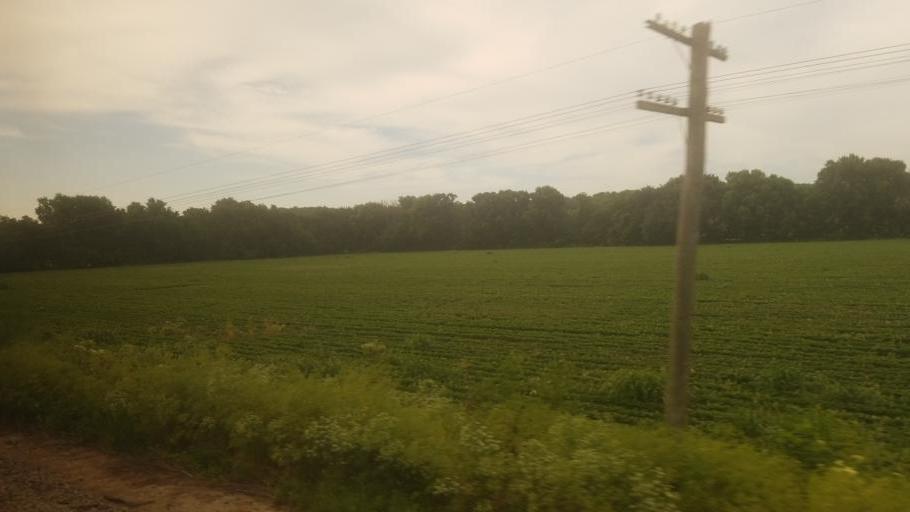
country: US
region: Kansas
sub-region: Shawnee County
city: Topeka
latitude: 39.0572
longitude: -95.5286
